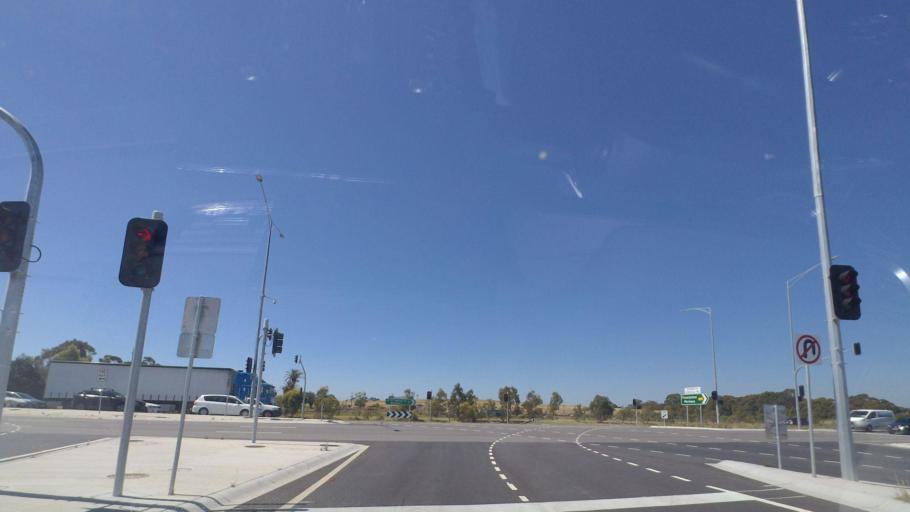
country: AU
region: Victoria
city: Heatherton
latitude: -37.9606
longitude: 145.1185
